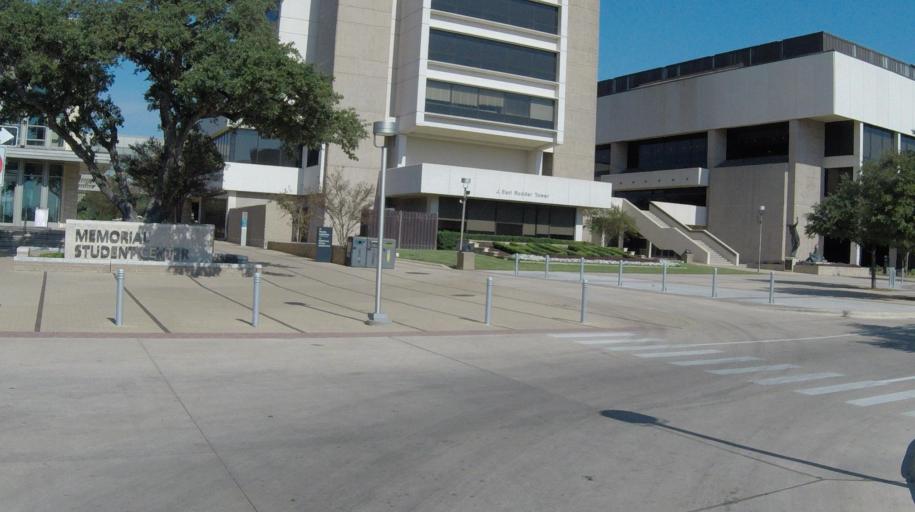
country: US
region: Texas
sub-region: Brazos County
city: College Station
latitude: 30.6122
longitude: -96.3401
